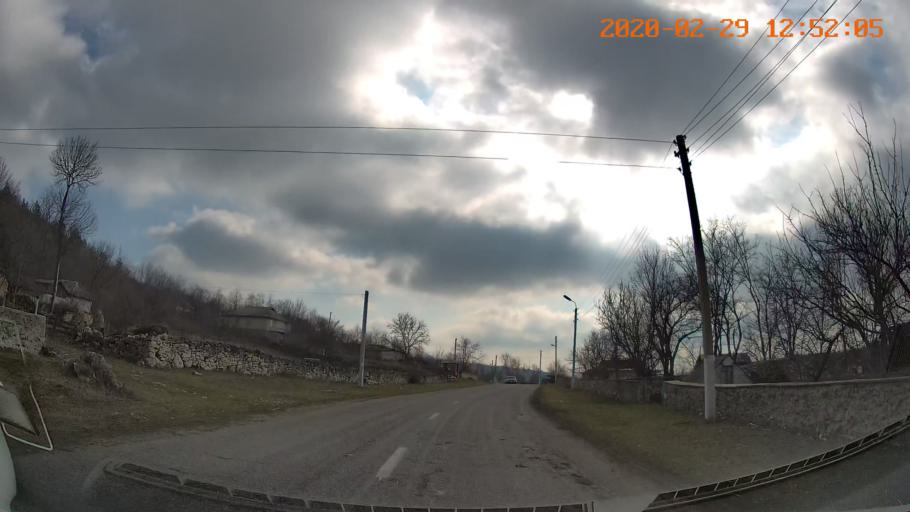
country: MD
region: Telenesti
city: Camenca
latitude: 48.1144
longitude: 28.7321
